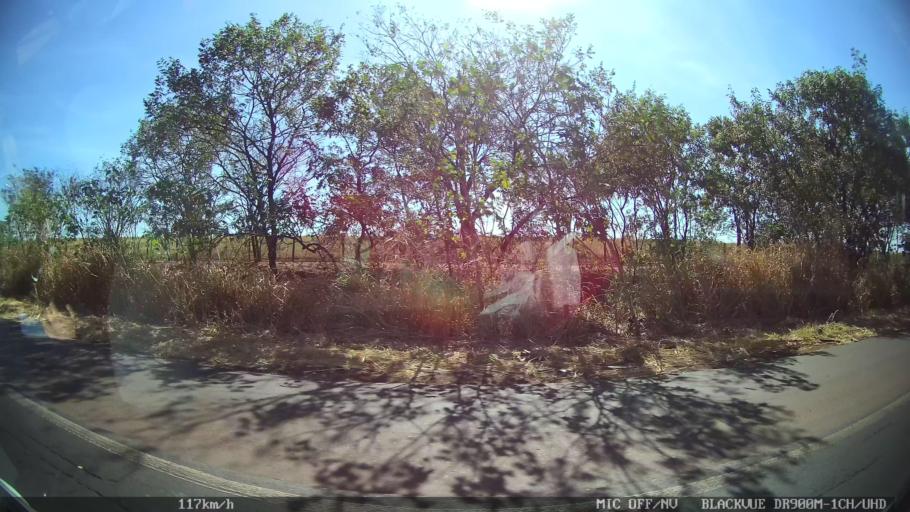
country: BR
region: Sao Paulo
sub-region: Barretos
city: Barretos
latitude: -20.4984
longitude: -48.5366
